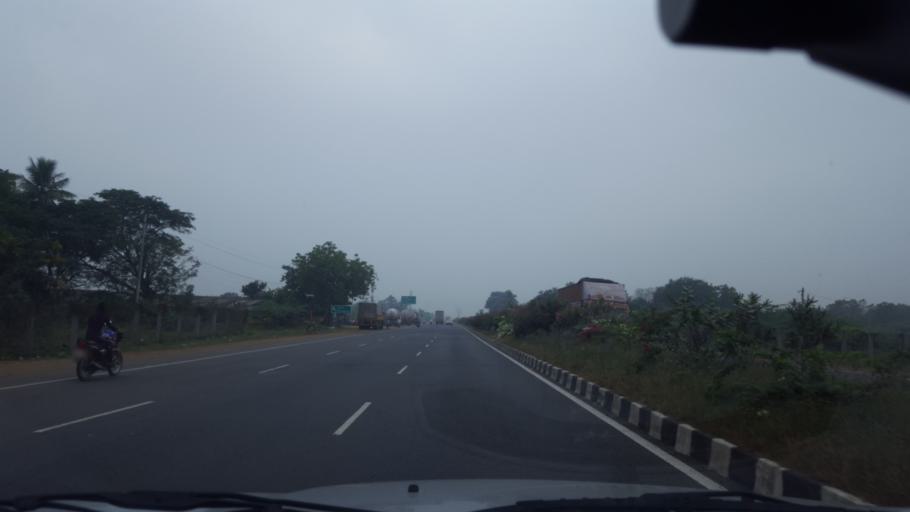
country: IN
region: Andhra Pradesh
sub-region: Prakasam
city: Ongole
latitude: 15.6084
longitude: 80.0271
